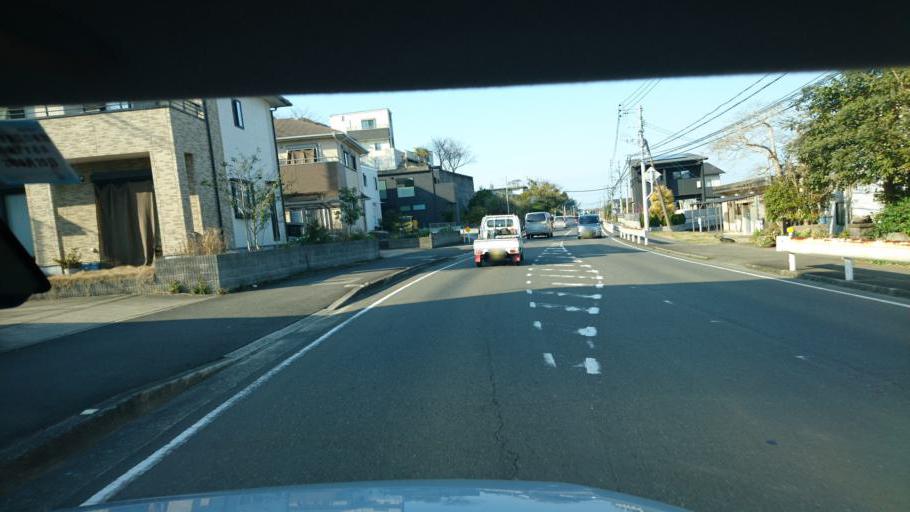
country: JP
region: Miyazaki
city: Miyazaki-shi
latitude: 31.9789
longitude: 131.4397
